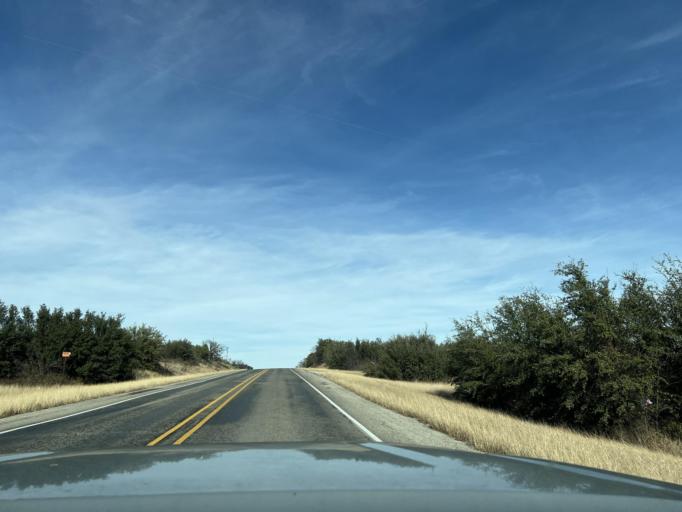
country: US
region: Texas
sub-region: Eastland County
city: Cisco
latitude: 32.4266
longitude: -98.9865
